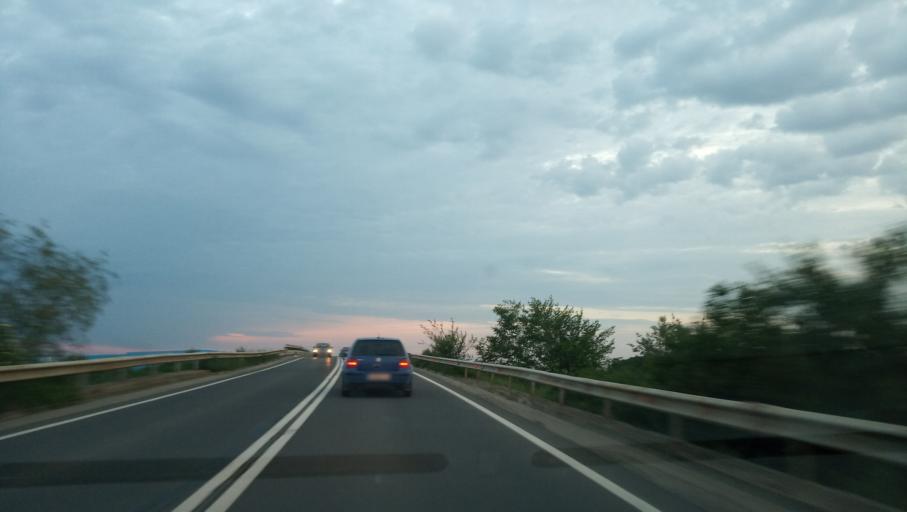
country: RO
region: Timis
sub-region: Comuna Sag
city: Sag
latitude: 45.6257
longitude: 21.1913
